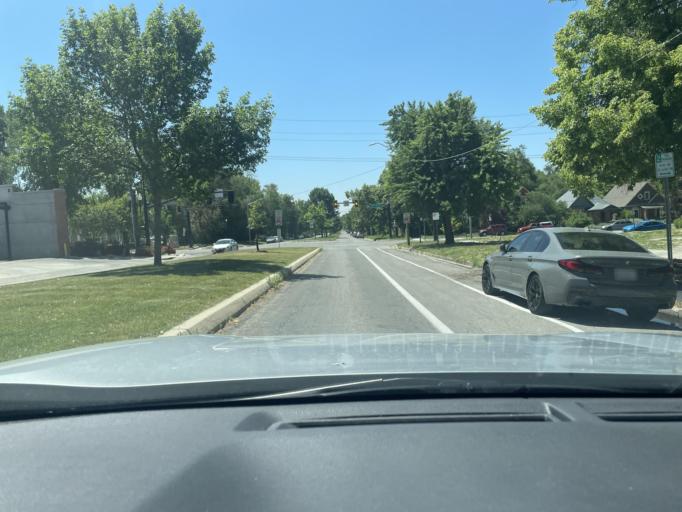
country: US
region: Utah
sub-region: Salt Lake County
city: Salt Lake City
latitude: 40.7570
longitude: -111.8740
